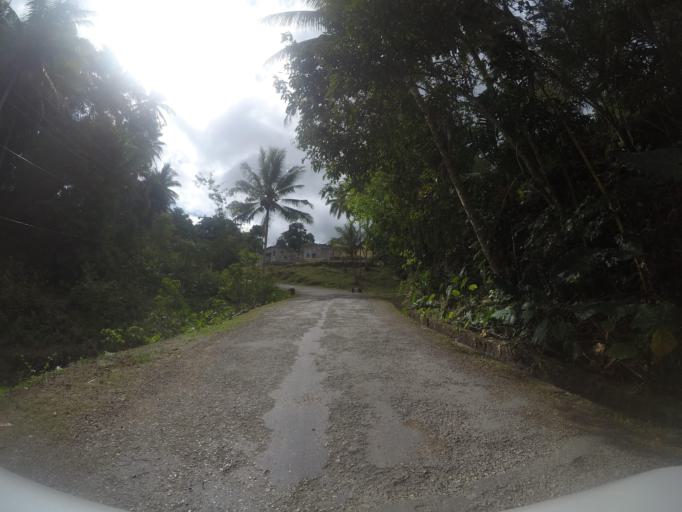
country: TL
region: Lautem
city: Lospalos
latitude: -8.5410
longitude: 126.9416
